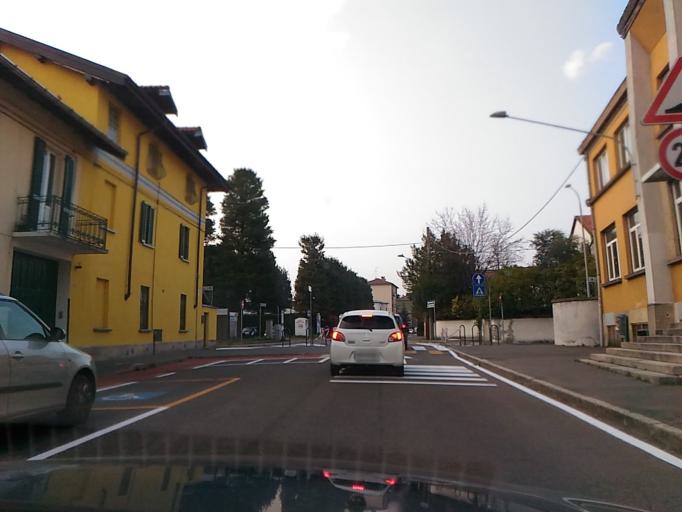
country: IT
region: Lombardy
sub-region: Provincia di Varese
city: Olgiate Olona
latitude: 45.6295
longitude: 8.8870
